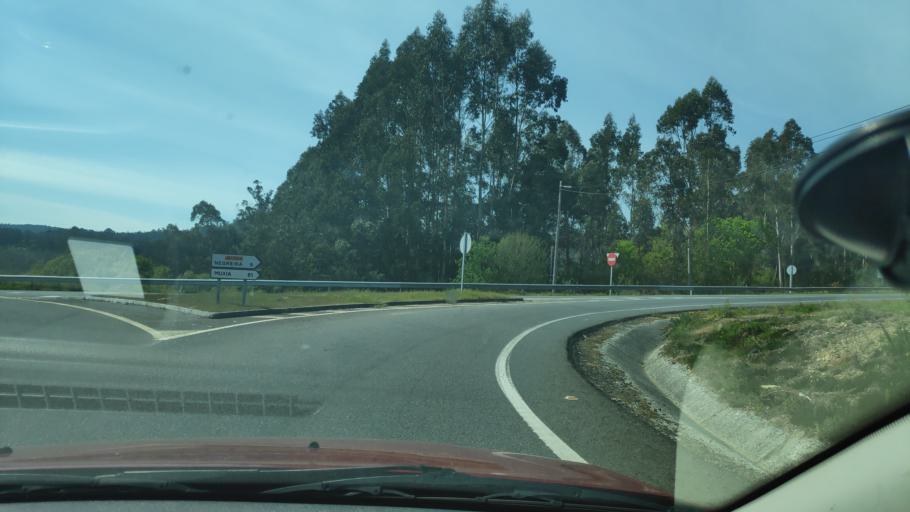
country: ES
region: Galicia
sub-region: Provincia da Coruna
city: Ames
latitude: 42.8698
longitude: -8.6581
